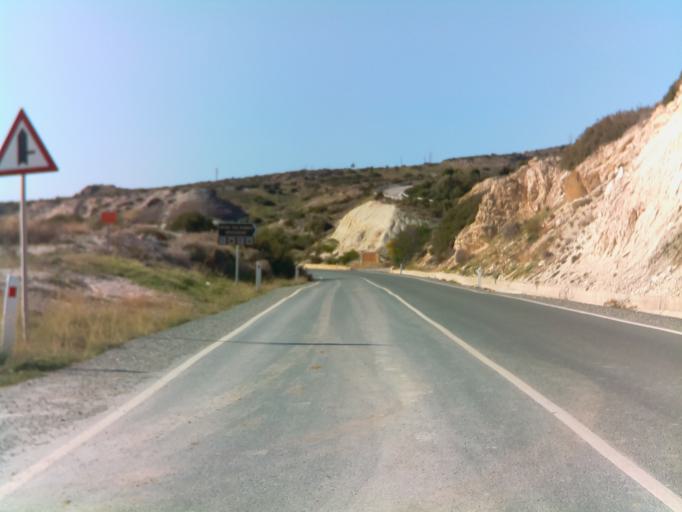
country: CY
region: Limassol
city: Pissouri
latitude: 34.6651
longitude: 32.6348
